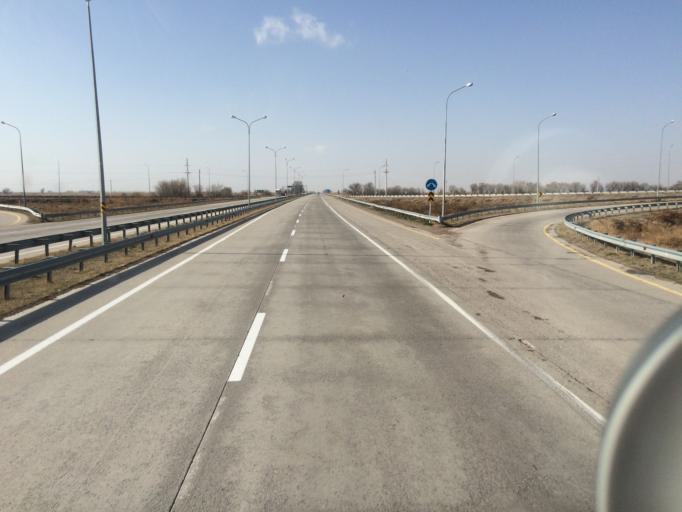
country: KZ
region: Zhambyl
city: Oytal
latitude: 42.9287
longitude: 73.2422
